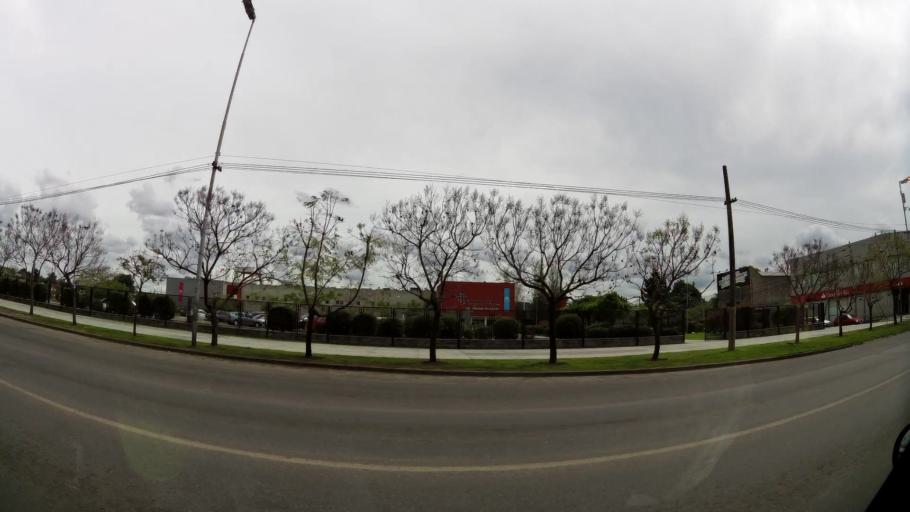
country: AR
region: Buenos Aires
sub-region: Partido de Quilmes
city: Quilmes
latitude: -34.7712
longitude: -58.2696
